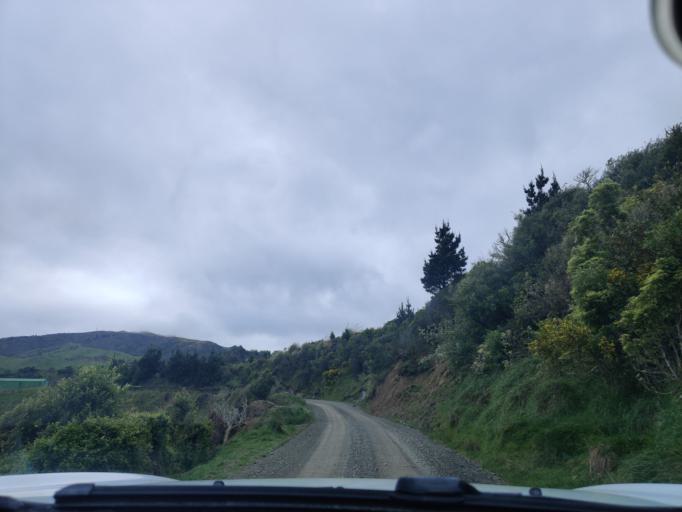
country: NZ
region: Manawatu-Wanganui
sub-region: Palmerston North City
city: Palmerston North
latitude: -40.2879
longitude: 175.8608
